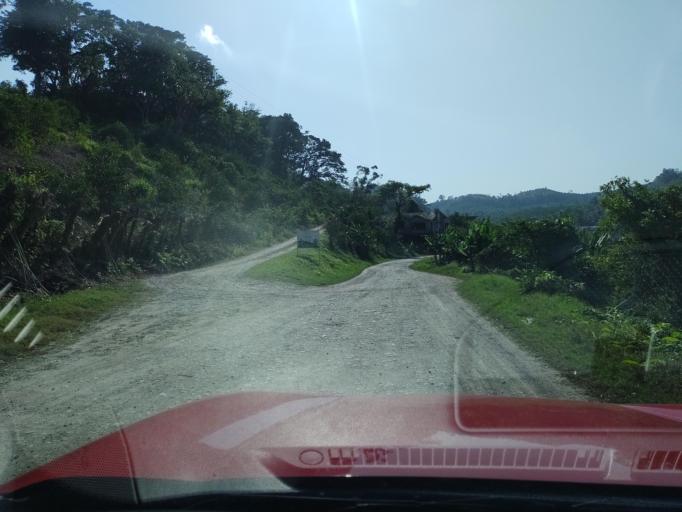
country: MX
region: Veracruz
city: Agua Dulce
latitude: 20.2911
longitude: -97.1835
